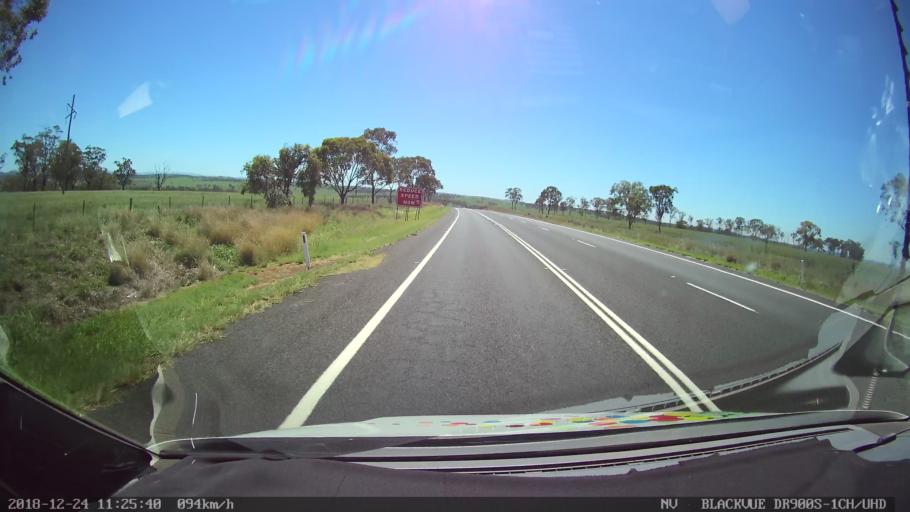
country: AU
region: New South Wales
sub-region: Upper Hunter Shire
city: Merriwa
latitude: -32.1697
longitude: 150.4194
